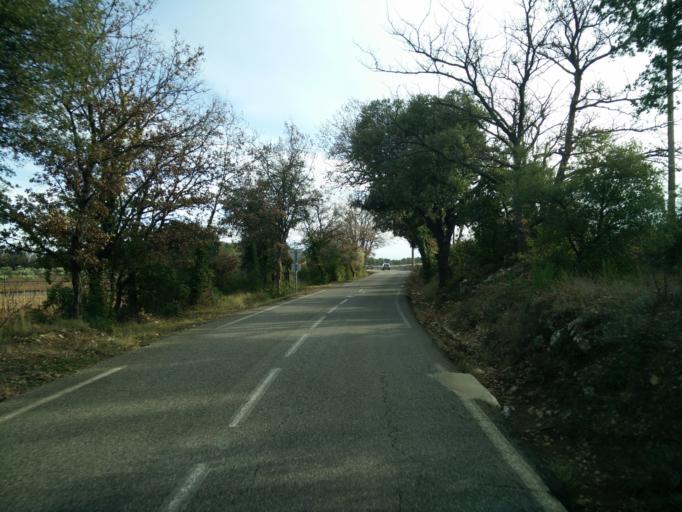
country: FR
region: Provence-Alpes-Cote d'Azur
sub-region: Departement du Var
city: Lorgues
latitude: 43.4659
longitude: 6.3885
